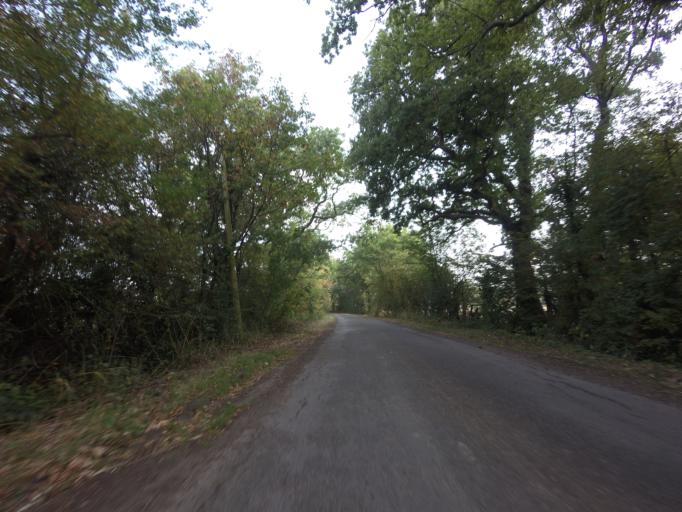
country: GB
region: England
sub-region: Kent
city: Tenterden
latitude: 51.1164
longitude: 0.6800
